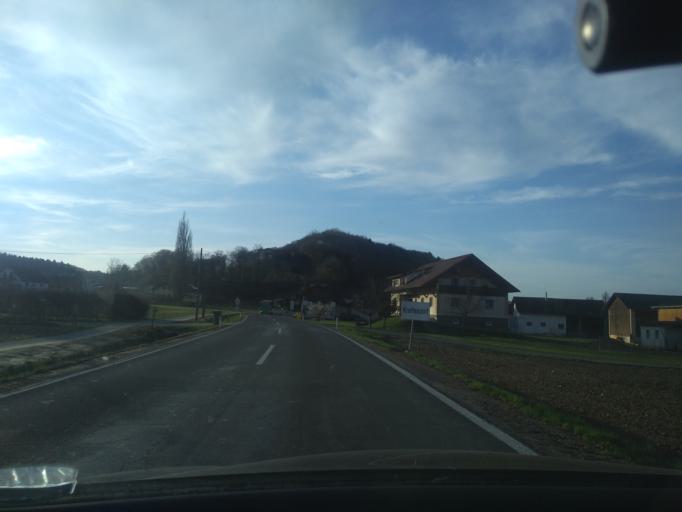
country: AT
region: Styria
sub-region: Politischer Bezirk Suedoststeiermark
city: Sankt Stefan im Rosental
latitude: 46.8907
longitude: 15.7200
